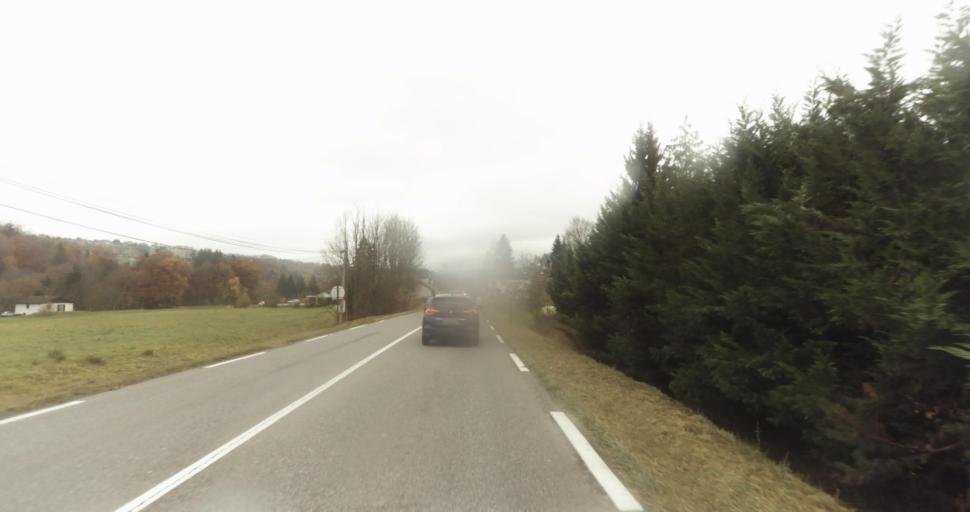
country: FR
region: Rhone-Alpes
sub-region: Departement de la Haute-Savoie
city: Saint-Martin-Bellevue
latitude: 45.9640
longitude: 6.1650
